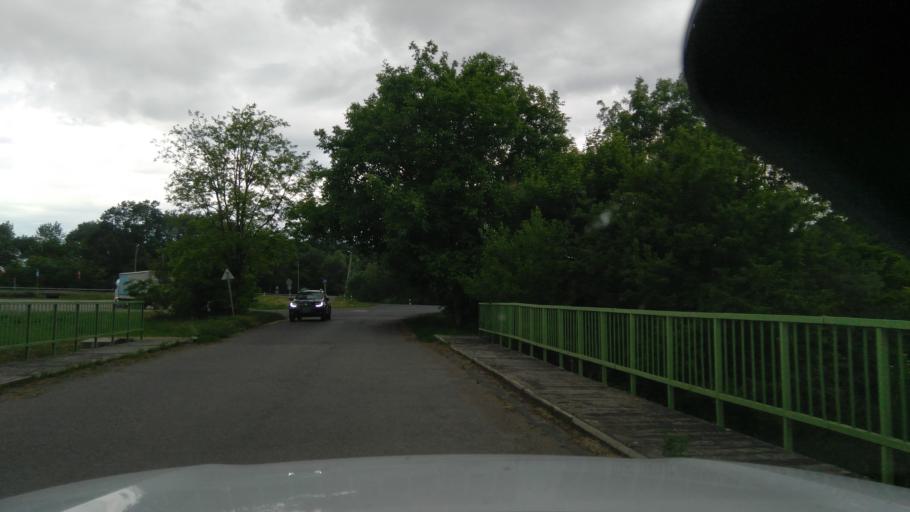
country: HU
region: Bekes
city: Bekescsaba
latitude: 46.6737
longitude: 21.1758
